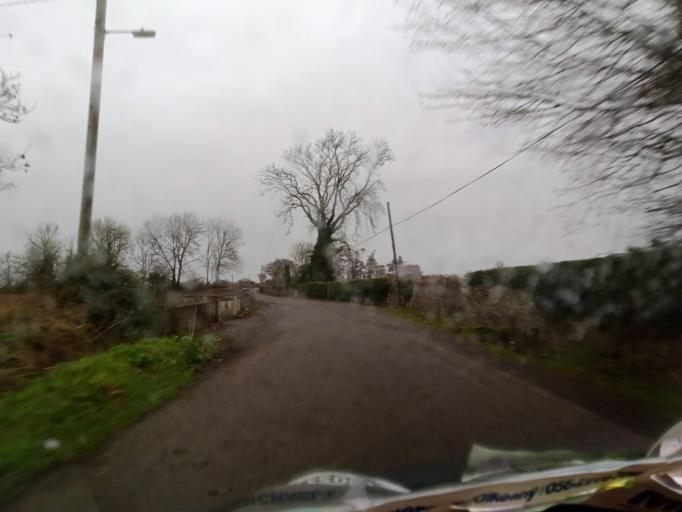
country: IE
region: Munster
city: Fethard
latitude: 52.5579
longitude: -7.7654
